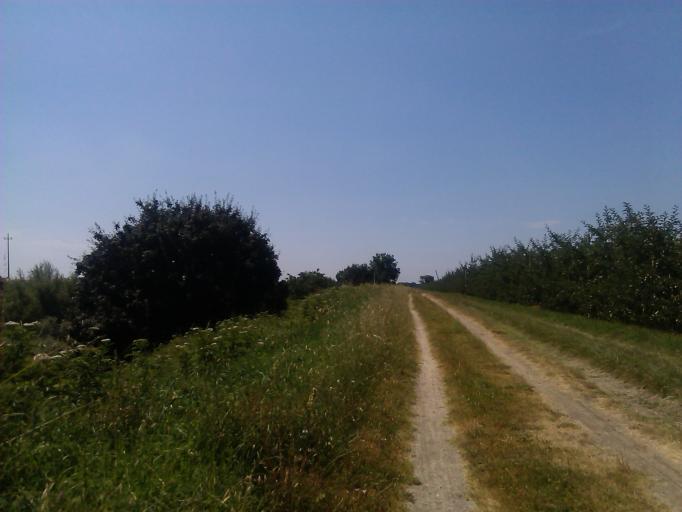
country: IT
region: Tuscany
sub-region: Province of Arezzo
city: Pieve al Toppo
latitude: 43.3761
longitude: 11.8245
